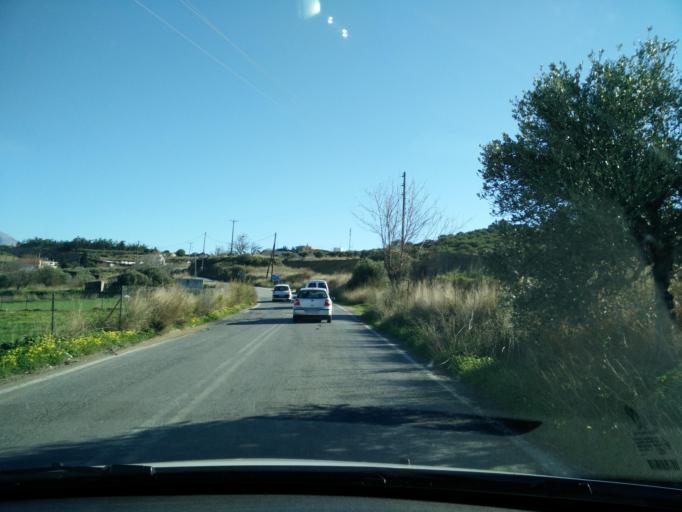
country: GR
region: Crete
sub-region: Nomos Irakleiou
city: Arkalochori
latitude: 35.1362
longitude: 25.2626
